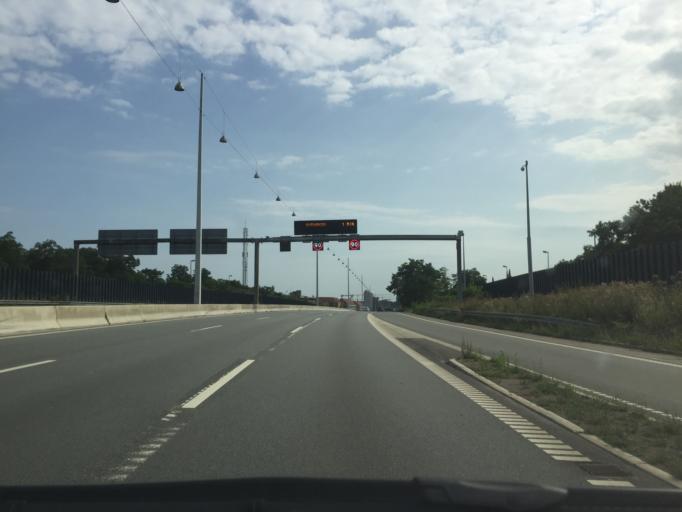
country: DK
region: Capital Region
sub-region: Gentofte Kommune
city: Charlottenlund
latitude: 55.7244
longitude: 12.5537
